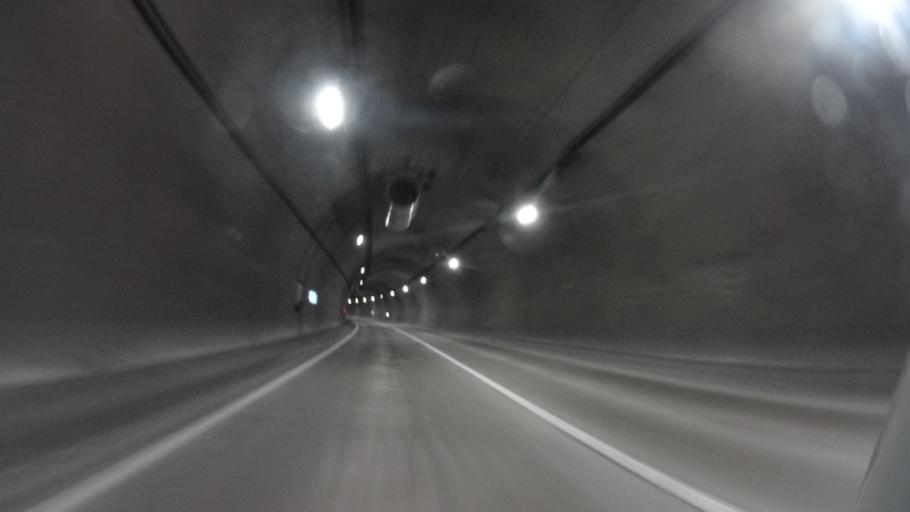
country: JP
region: Fukui
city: Tsuruga
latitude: 35.6176
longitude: 136.0835
